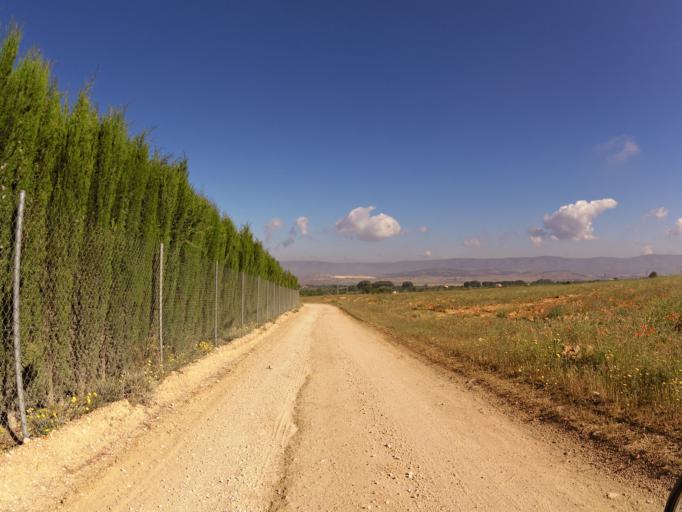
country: ES
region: Valencia
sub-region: Provincia de Alicante
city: Biar
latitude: 38.6386
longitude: -0.7680
